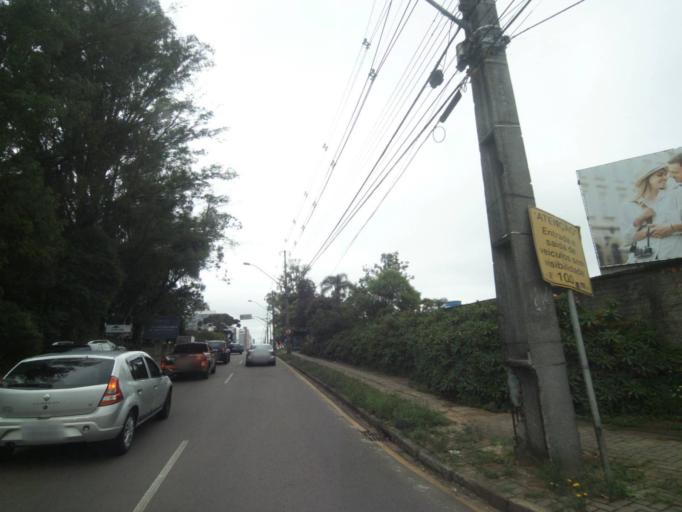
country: BR
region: Parana
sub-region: Curitiba
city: Curitiba
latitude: -25.4386
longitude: -49.3106
